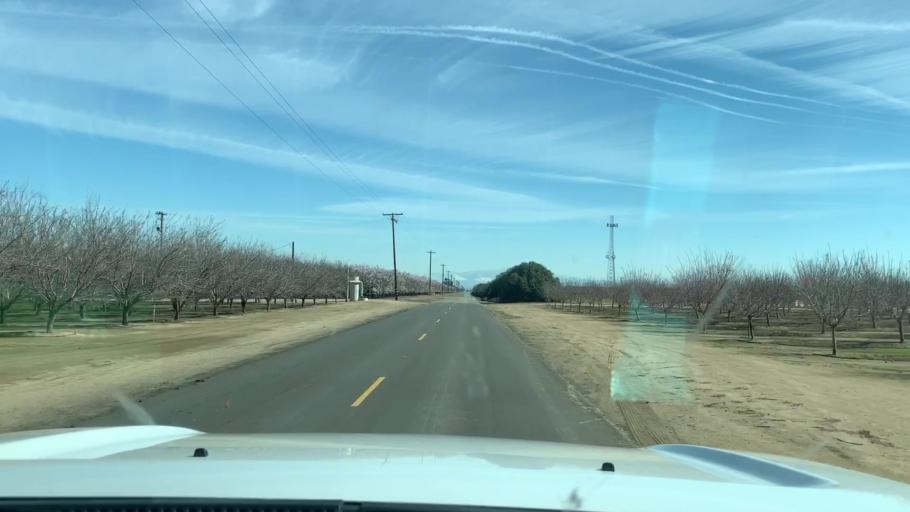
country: US
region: California
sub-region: Kern County
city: Shafter
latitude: 35.4853
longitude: -119.2707
